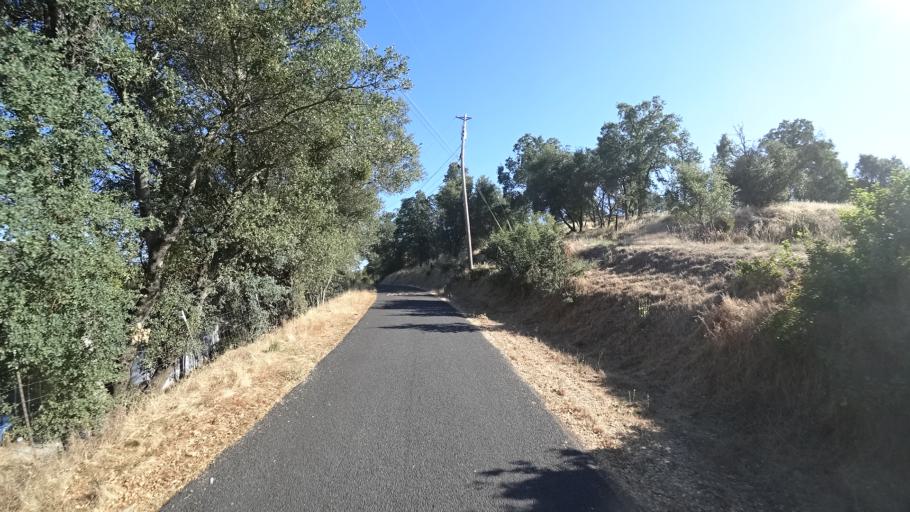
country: US
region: California
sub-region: Calaveras County
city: San Andreas
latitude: 38.2318
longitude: -120.7126
